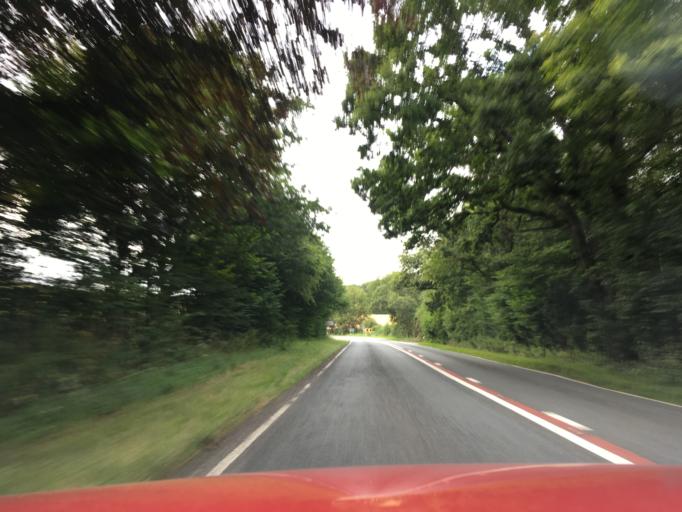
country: GB
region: England
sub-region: Hampshire
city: Four Marks
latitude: 51.0305
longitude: -1.0336
